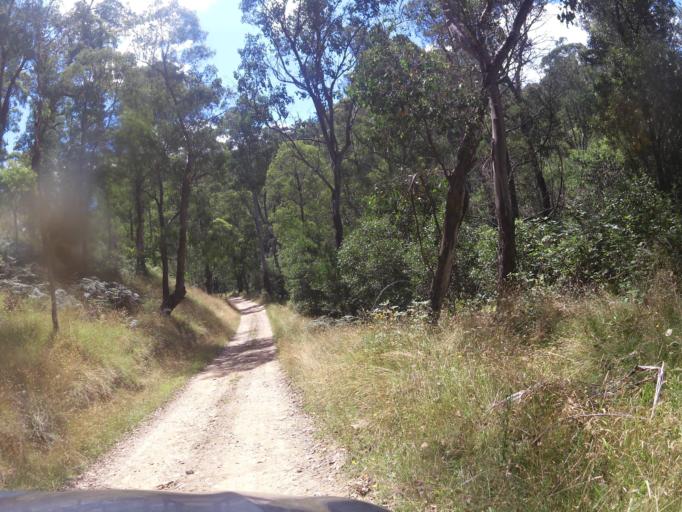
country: AU
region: Victoria
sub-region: Alpine
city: Mount Beauty
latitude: -36.7820
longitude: 147.0737
